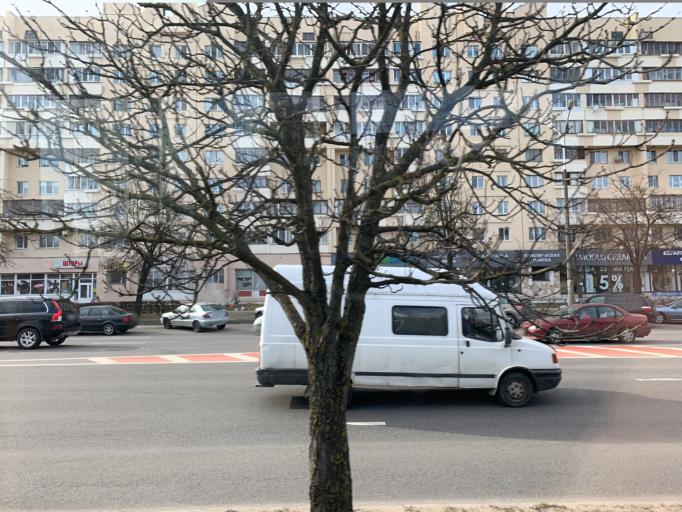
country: BY
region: Minsk
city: Minsk
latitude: 53.9480
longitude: 27.6144
